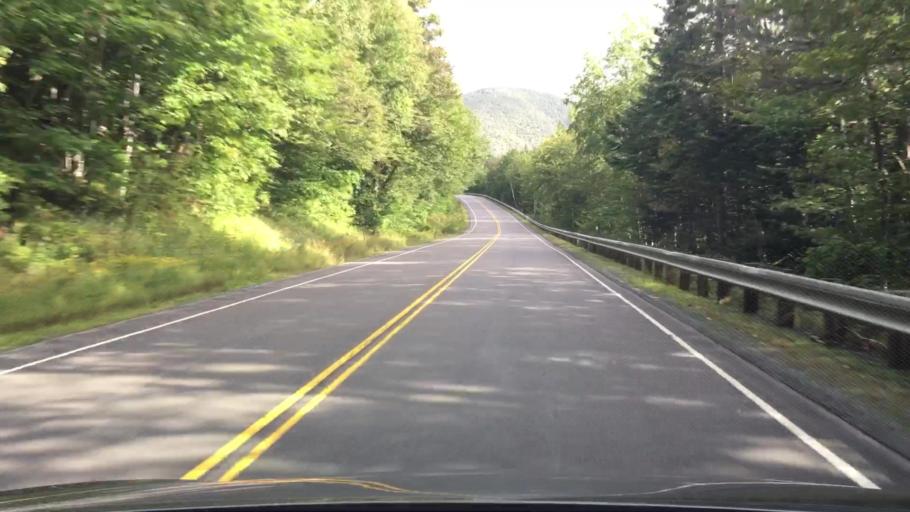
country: US
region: New Hampshire
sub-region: Grafton County
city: Woodstock
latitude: 44.0388
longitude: -71.5220
